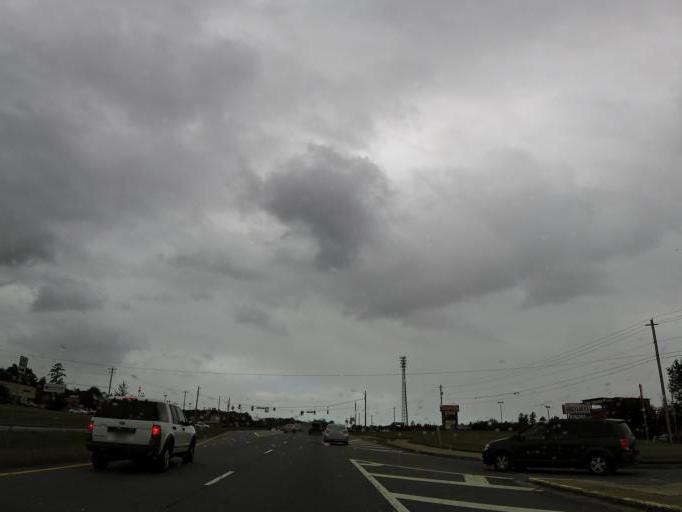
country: US
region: Georgia
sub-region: Cobb County
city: Acworth
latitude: 34.0350
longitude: -84.6781
